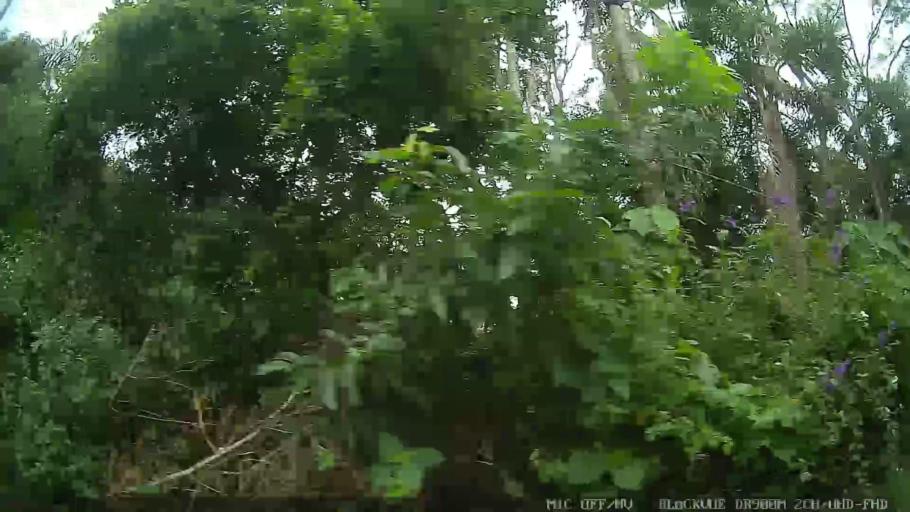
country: BR
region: Sao Paulo
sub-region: Iguape
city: Iguape
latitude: -24.6899
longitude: -47.5235
